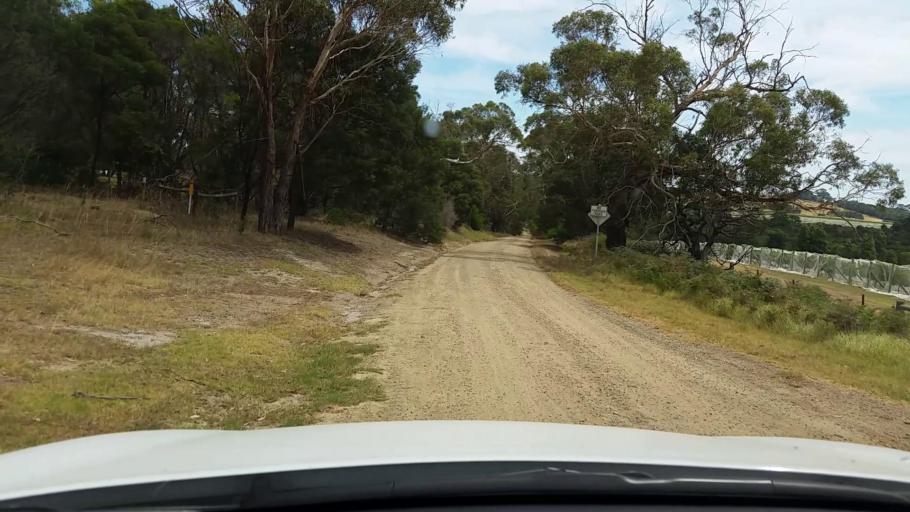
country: AU
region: Victoria
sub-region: Mornington Peninsula
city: Mount Martha
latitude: -38.2862
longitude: 145.0627
